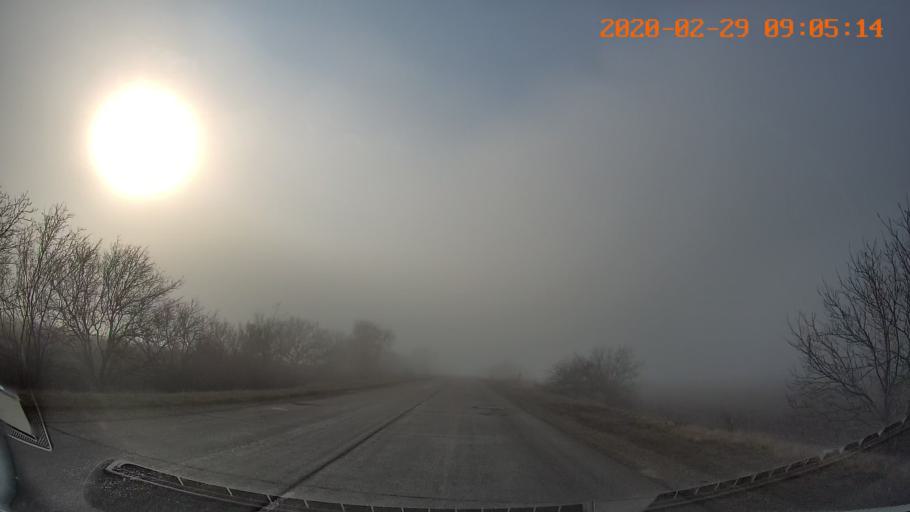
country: MD
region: Telenesti
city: Tiraspolul Nou
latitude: 46.8920
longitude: 29.7394
